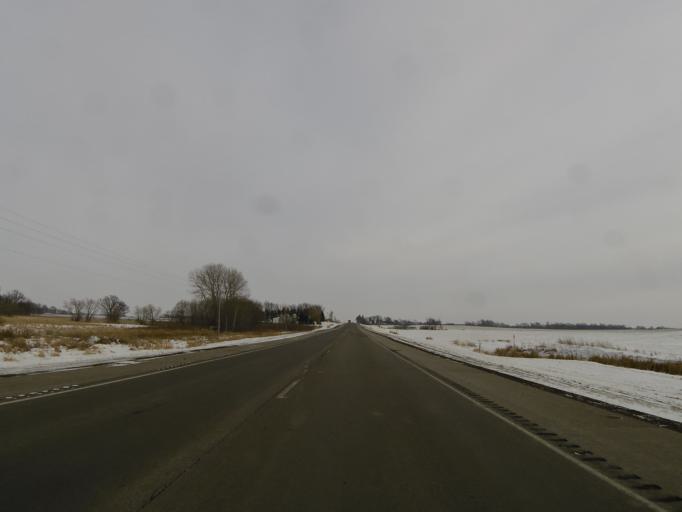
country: US
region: Minnesota
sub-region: McLeod County
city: Lester Prairie
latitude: 44.9067
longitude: -94.1698
